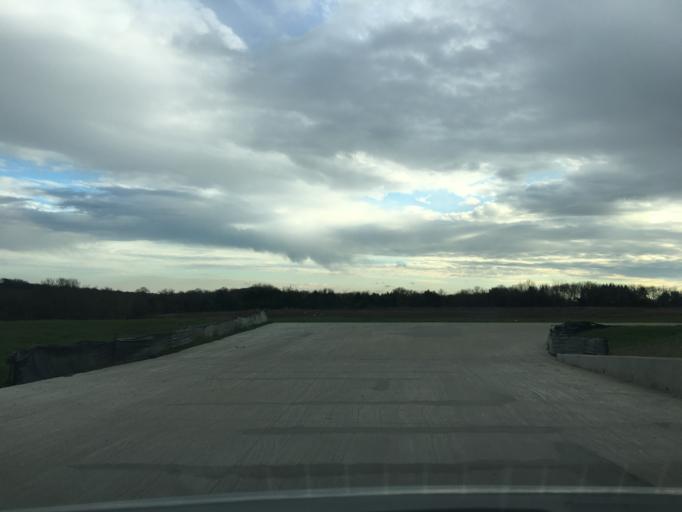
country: US
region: Texas
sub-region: Collin County
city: Anna
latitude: 33.3450
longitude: -96.5820
